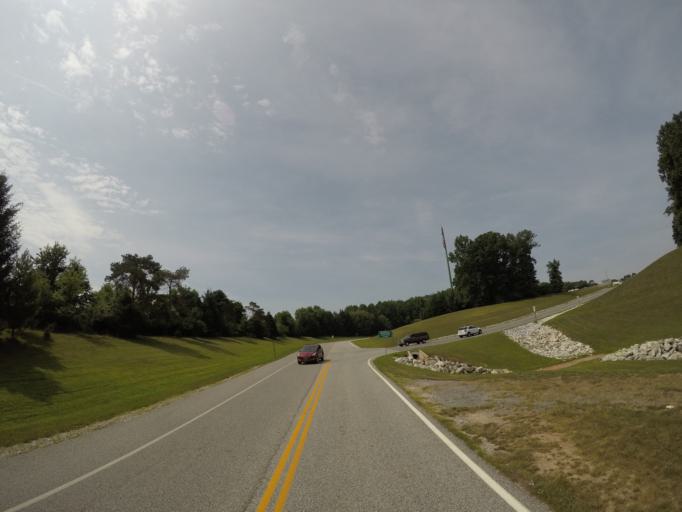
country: US
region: Maryland
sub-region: Howard County
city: Columbia
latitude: 39.3057
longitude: -76.9010
